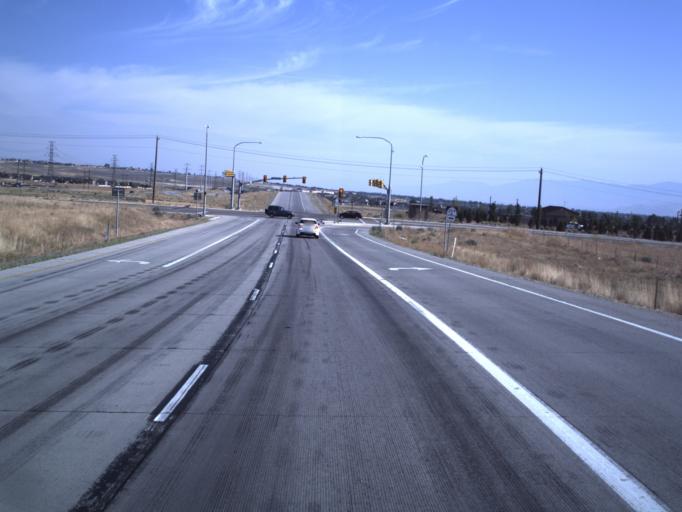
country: US
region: Utah
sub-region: Salt Lake County
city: Oquirrh
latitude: 40.5865
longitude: -112.0278
